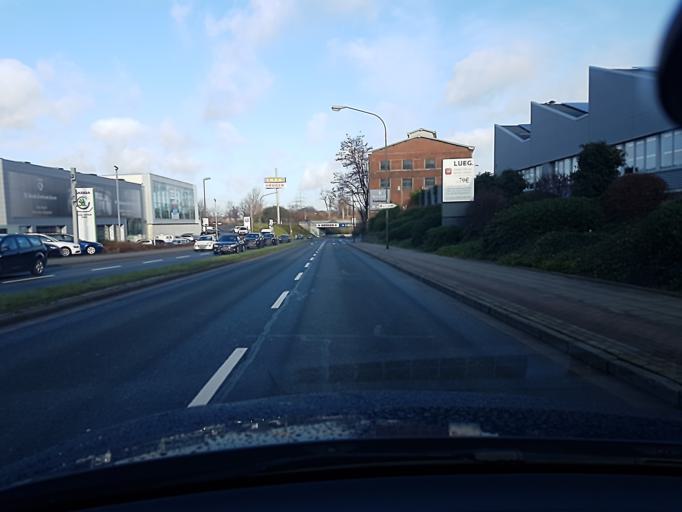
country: DE
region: North Rhine-Westphalia
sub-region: Regierungsbezirk Dusseldorf
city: Essen
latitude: 51.4601
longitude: 6.9970
